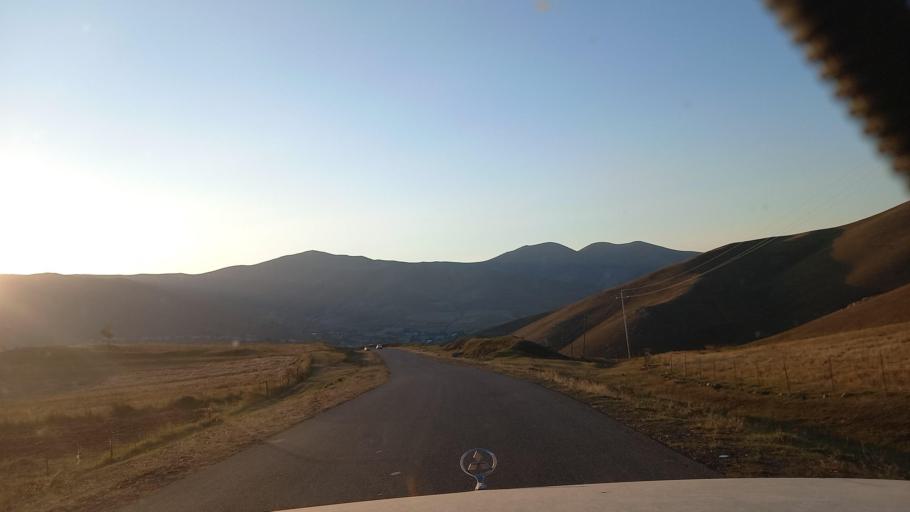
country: AZ
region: Gadabay Rayon
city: Ariqdam
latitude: 40.6822
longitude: 45.7789
